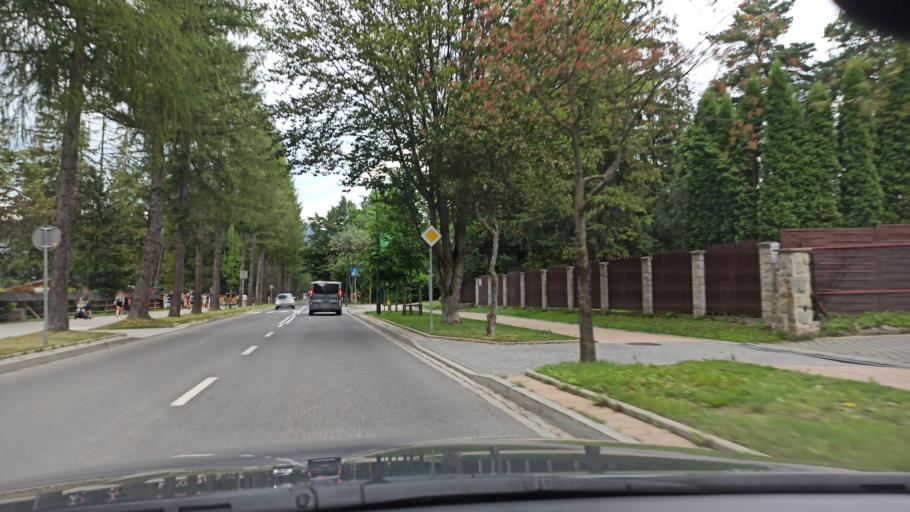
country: PL
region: Lesser Poland Voivodeship
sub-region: Powiat tatrzanski
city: Zakopane
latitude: 49.2857
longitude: 19.9632
